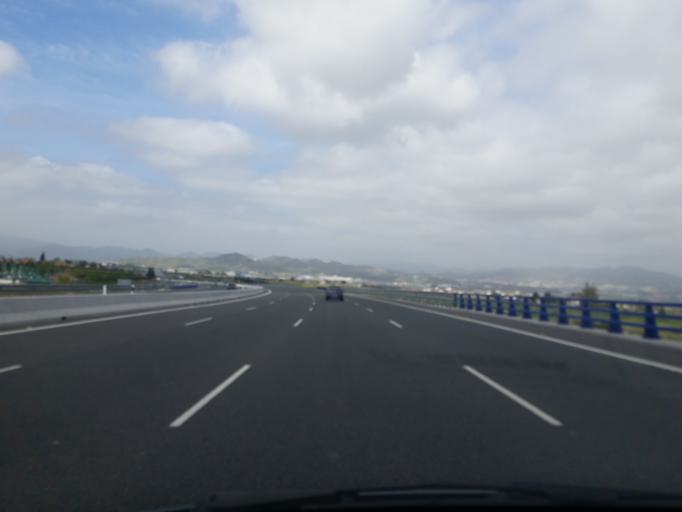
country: ES
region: Andalusia
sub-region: Provincia de Malaga
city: Alhaurin de la Torre
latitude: 36.6769
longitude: -4.5261
